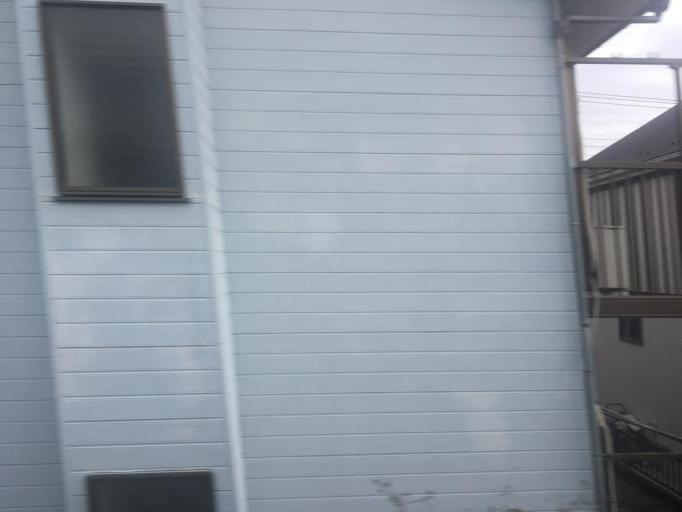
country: JP
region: Tokyo
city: Fussa
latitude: 35.7299
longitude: 139.3395
